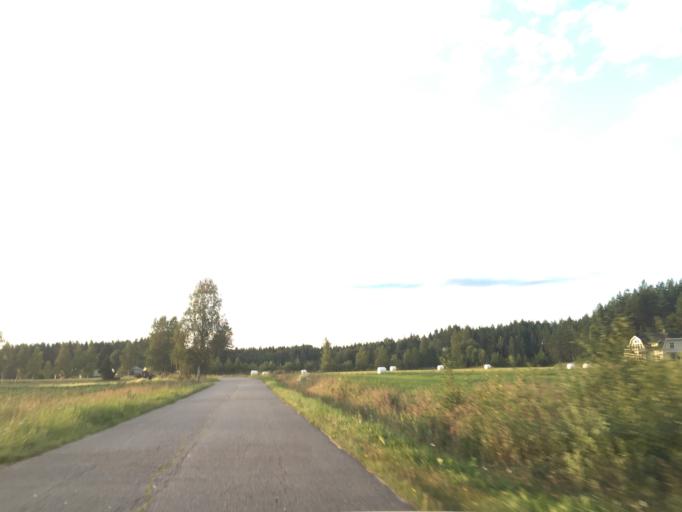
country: NO
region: Akershus
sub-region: Nes
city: Fjellfoten
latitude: 60.0953
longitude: 11.4897
